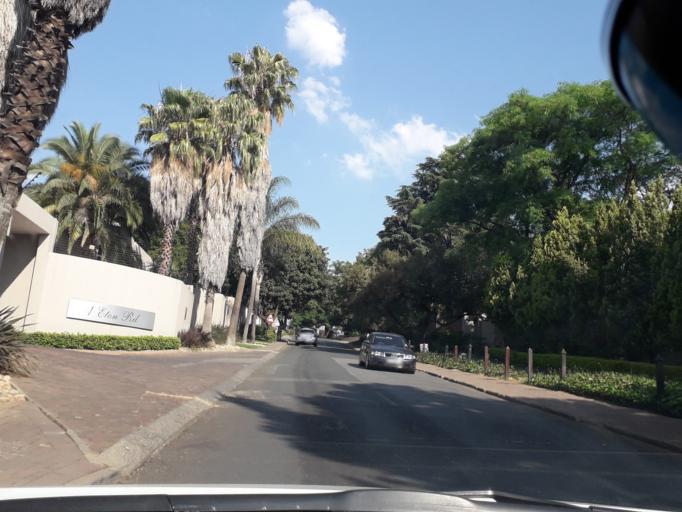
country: ZA
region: Gauteng
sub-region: City of Johannesburg Metropolitan Municipality
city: Johannesburg
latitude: -26.1156
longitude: 28.0441
